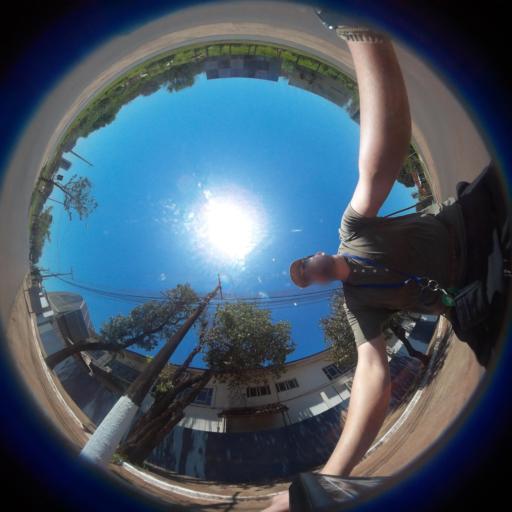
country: BR
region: Mato Grosso do Sul
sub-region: Ponta Pora
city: Ponta Pora
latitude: -22.5274
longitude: -55.7337
